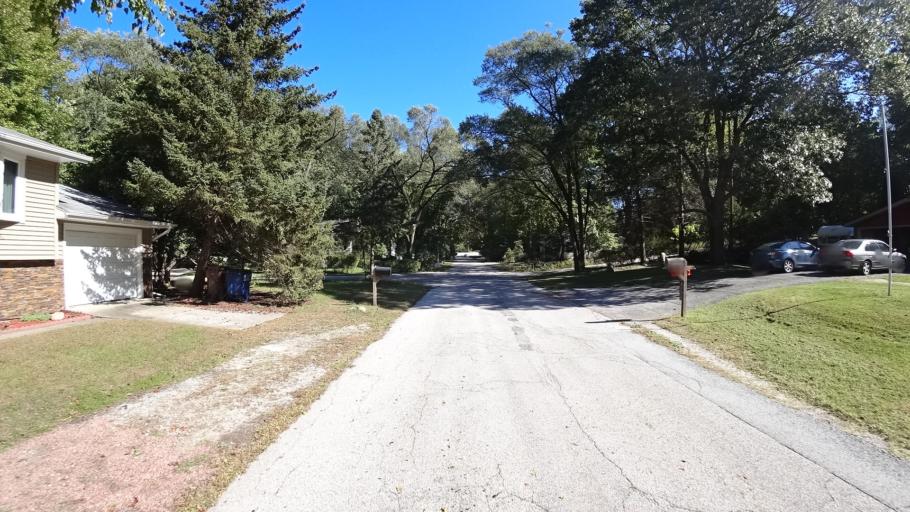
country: US
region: Indiana
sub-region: LaPorte County
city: Long Beach
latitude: 41.7527
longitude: -86.8185
